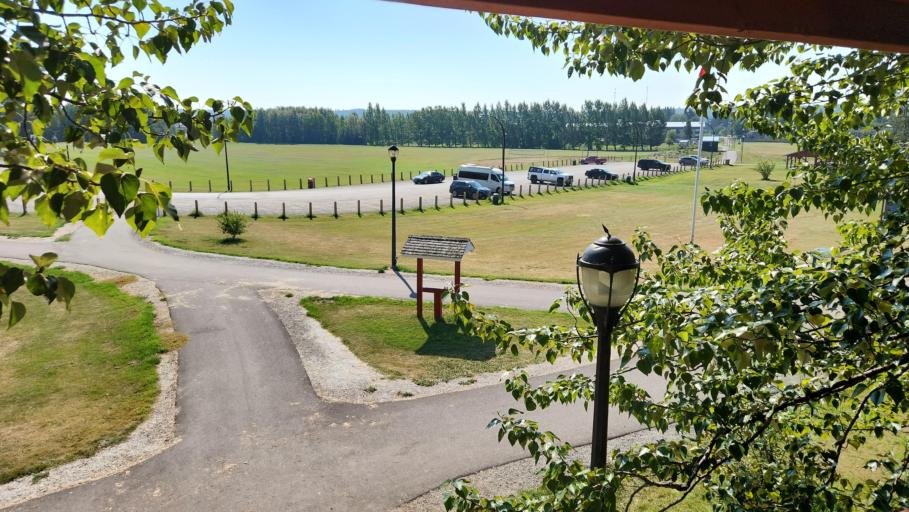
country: CA
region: British Columbia
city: Vanderhoof
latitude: 54.0253
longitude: -124.0134
